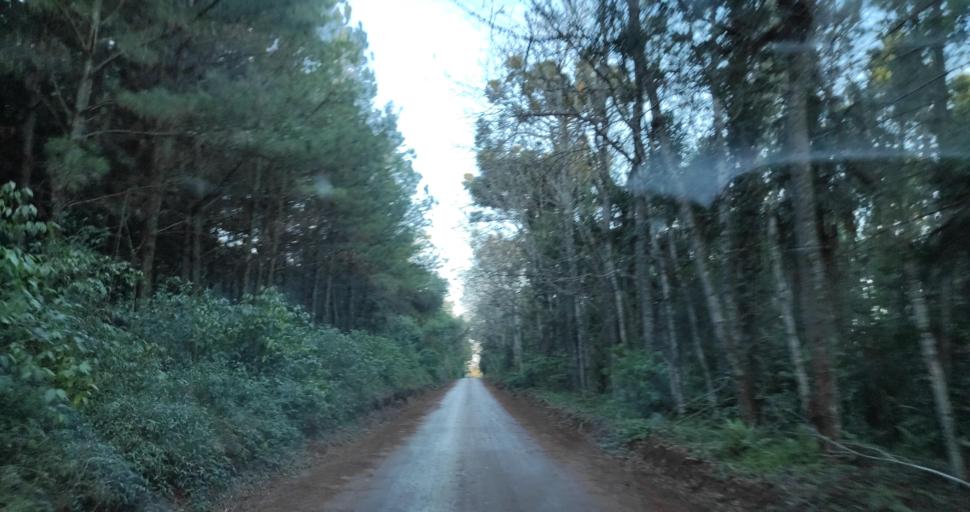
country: AR
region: Misiones
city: Capiovi
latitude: -26.8772
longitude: -55.0933
